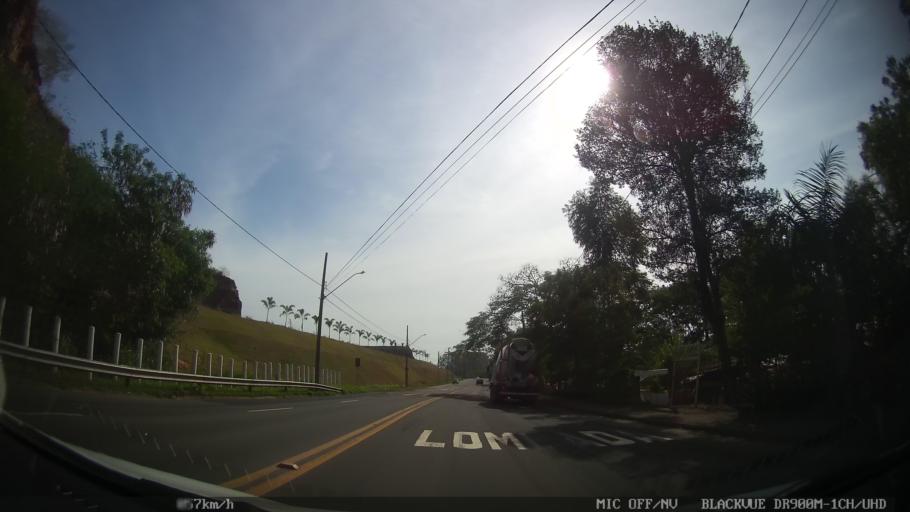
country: BR
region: Sao Paulo
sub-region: Piracicaba
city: Piracicaba
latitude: -22.7117
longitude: -47.6773
